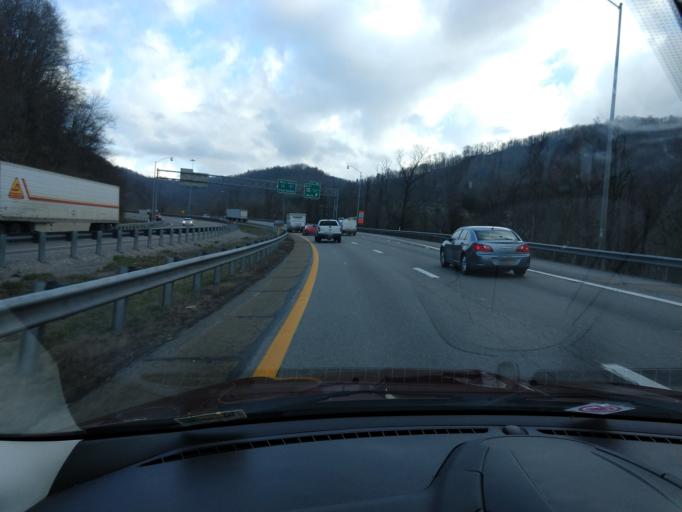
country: US
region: West Virginia
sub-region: Kanawha County
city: Rand
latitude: 38.3143
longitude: -81.5547
